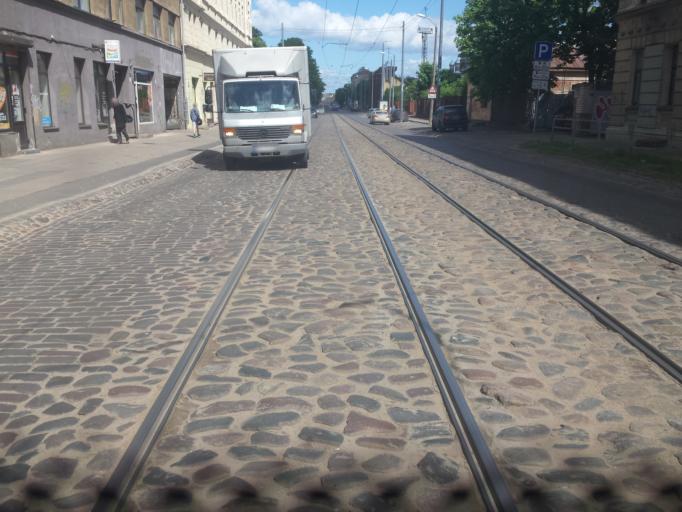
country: LV
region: Riga
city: Riga
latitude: 56.9610
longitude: 24.1409
